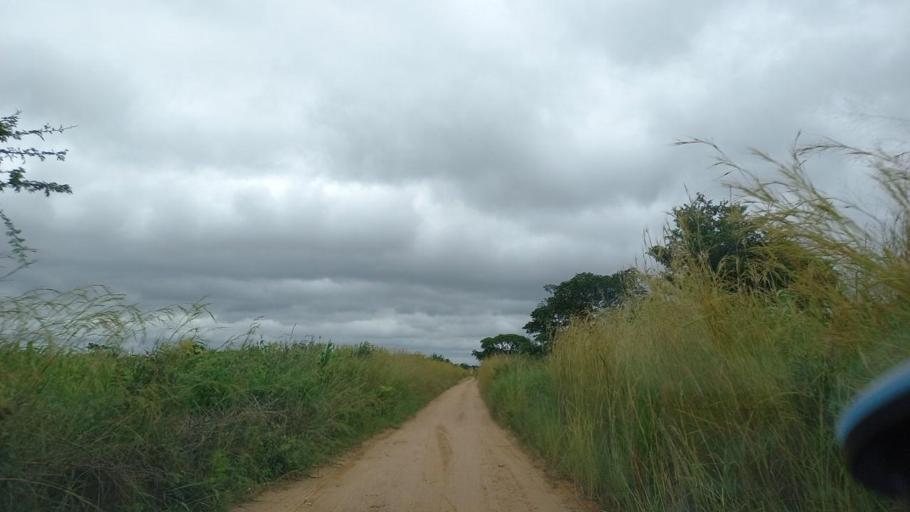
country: ZM
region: Lusaka
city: Lusaka
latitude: -15.1345
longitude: 28.3686
